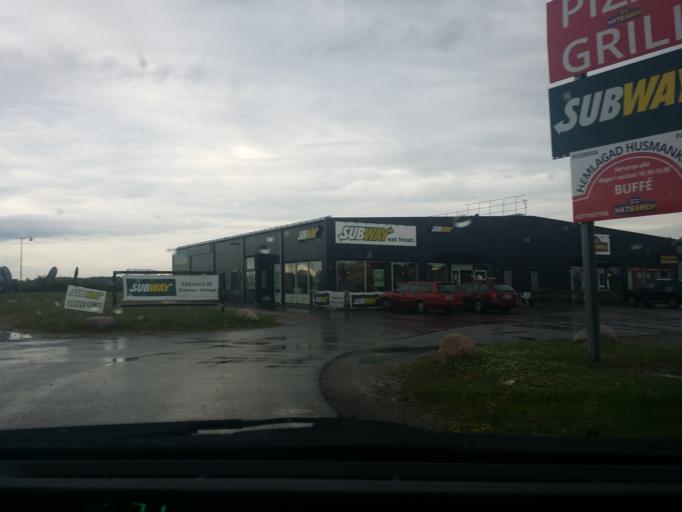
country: SE
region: Vaestmanland
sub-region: Arboga Kommun
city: Arboga
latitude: 59.4264
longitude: 15.8294
